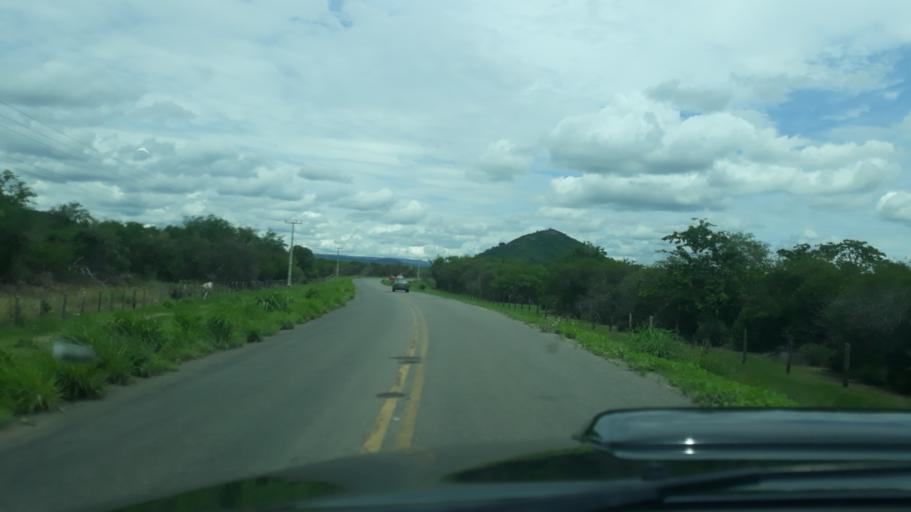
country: BR
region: Bahia
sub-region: Guanambi
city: Guanambi
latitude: -14.1674
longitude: -42.8096
